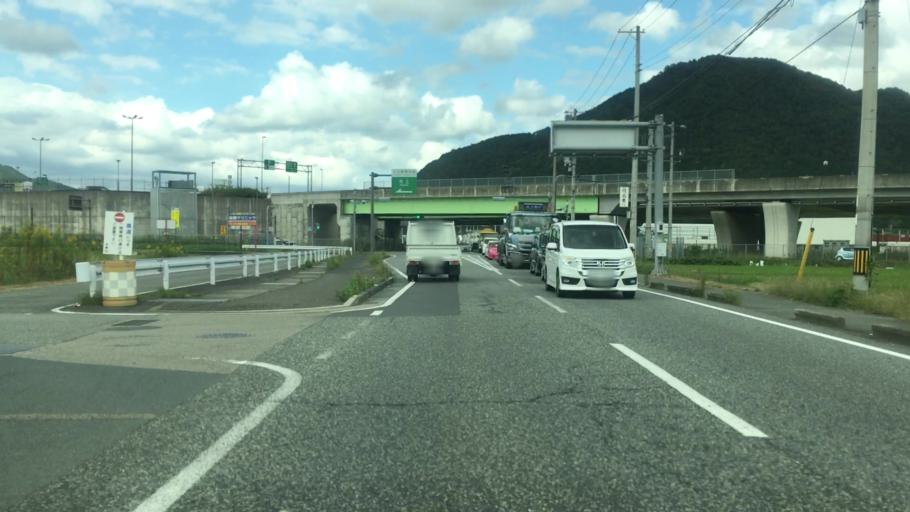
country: JP
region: Kyoto
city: Fukuchiyama
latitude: 35.1594
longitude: 135.0478
